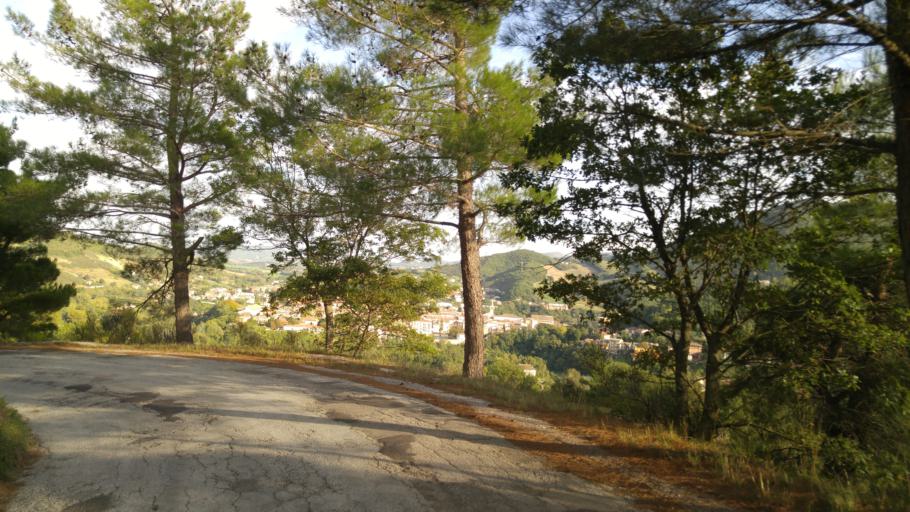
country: IT
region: The Marches
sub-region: Provincia di Pesaro e Urbino
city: Cagli
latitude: 43.5507
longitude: 12.6383
